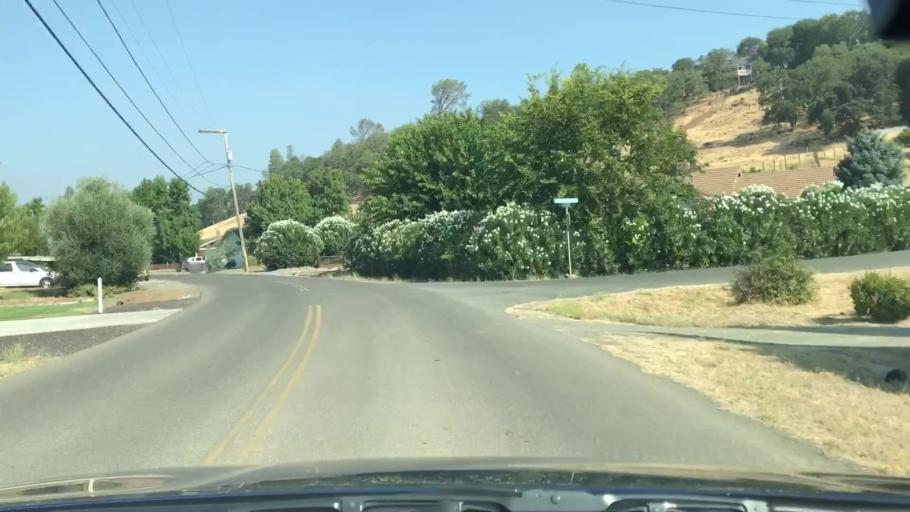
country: US
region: California
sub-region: Lake County
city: Hidden Valley Lake
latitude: 38.7889
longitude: -122.5435
